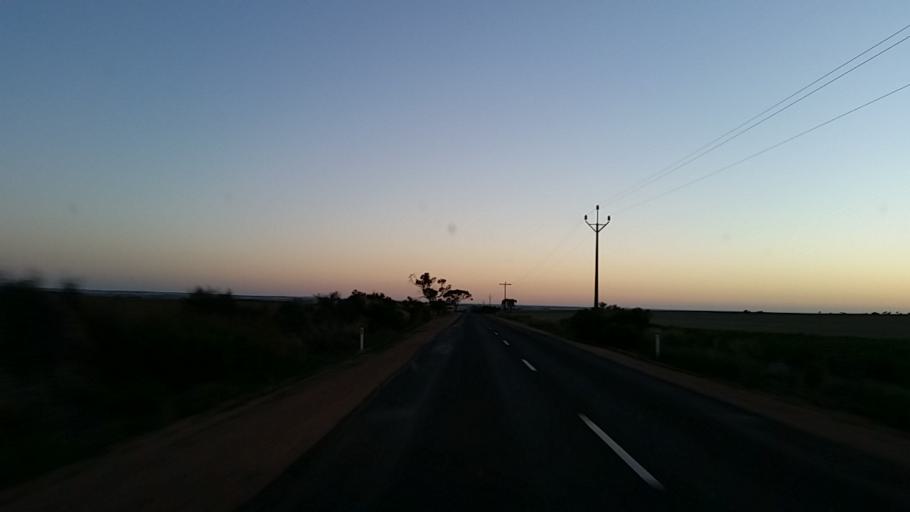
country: AU
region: South Australia
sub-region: Wakefield
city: Balaklava
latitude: -33.9918
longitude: 138.5129
